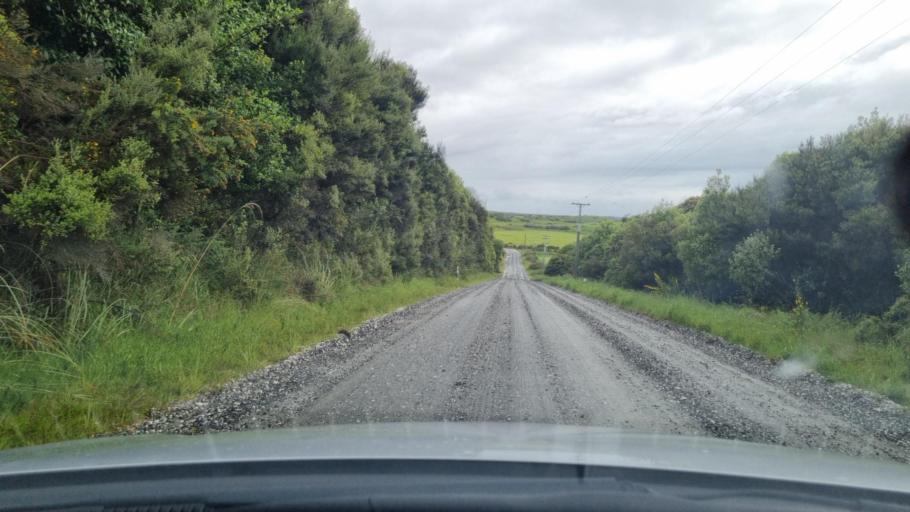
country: NZ
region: Southland
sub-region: Invercargill City
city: Bluff
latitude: -46.5234
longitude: 168.2713
